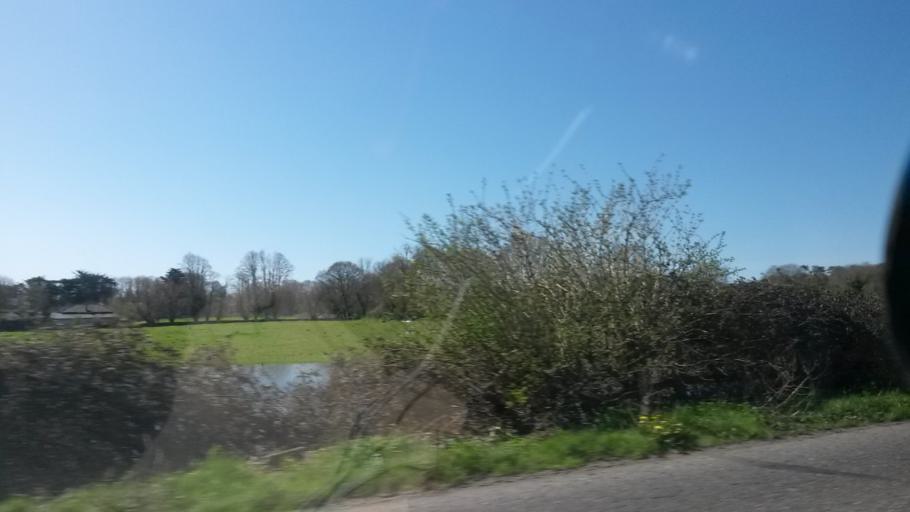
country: IE
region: Munster
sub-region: County Cork
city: Blarney
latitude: 51.8958
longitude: -8.5398
